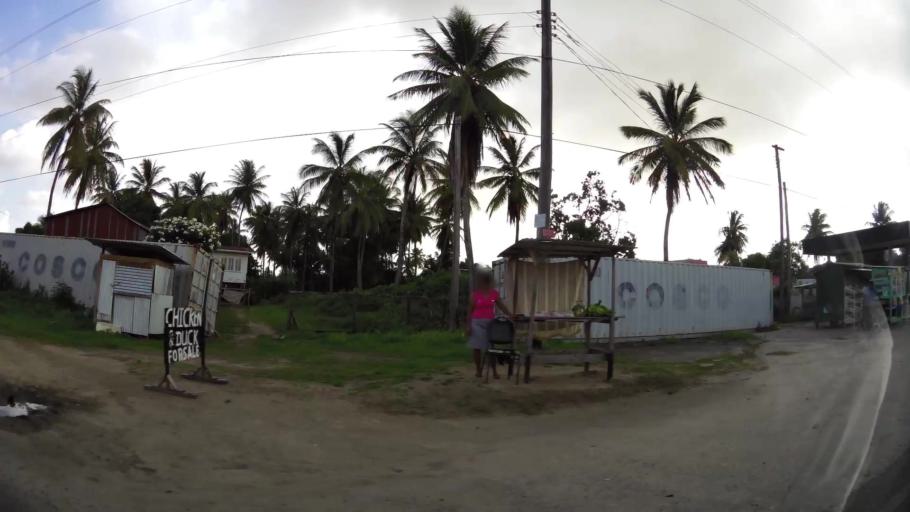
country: GY
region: Demerara-Mahaica
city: Georgetown
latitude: 6.7873
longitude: -58.0170
